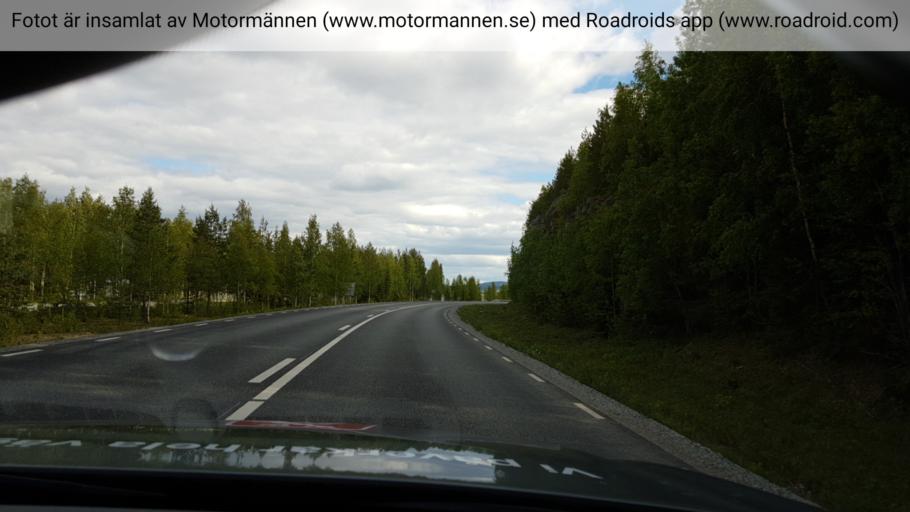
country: SE
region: Jaemtland
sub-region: Stroemsunds Kommun
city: Stroemsund
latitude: 64.1828
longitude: 15.6528
